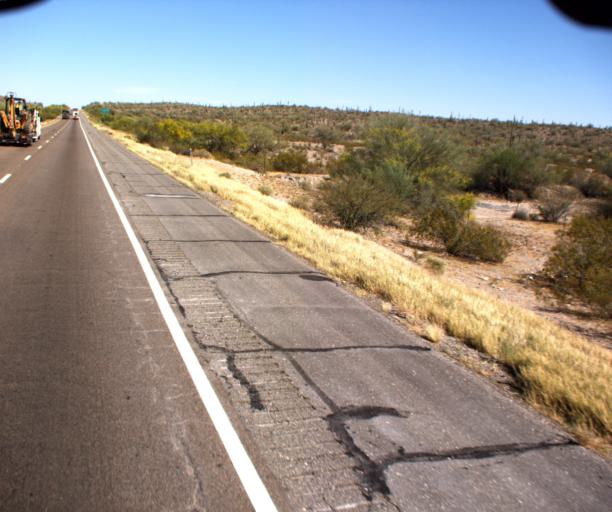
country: US
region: Arizona
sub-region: Pinal County
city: Maricopa
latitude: 32.8499
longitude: -112.3460
